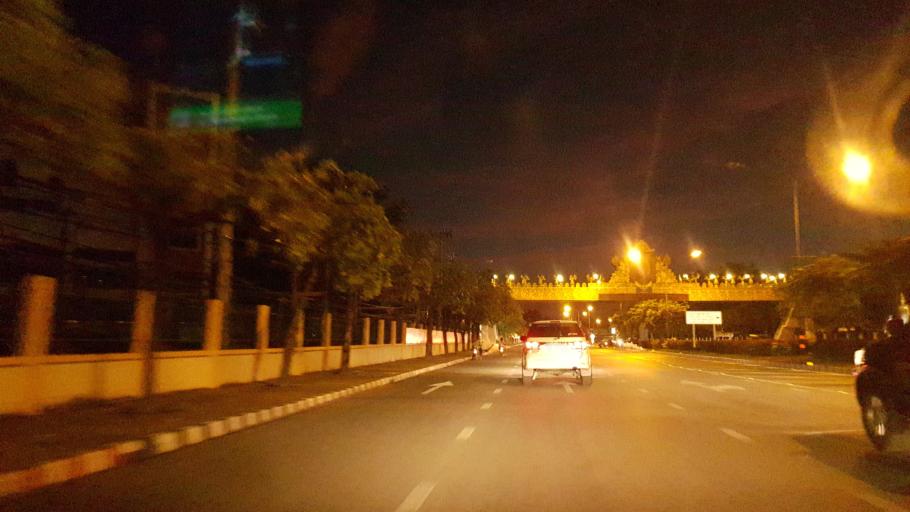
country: TH
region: Phitsanulok
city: Phitsanulok
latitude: 16.8126
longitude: 100.2719
